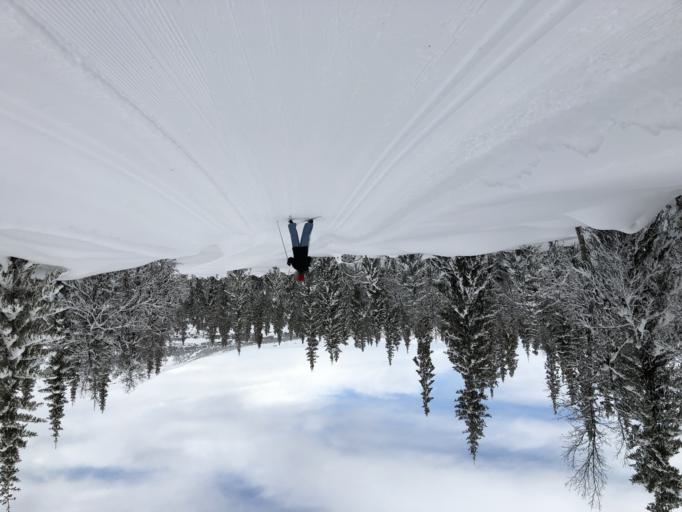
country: NO
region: Oppland
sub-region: Gausdal
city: Segalstad bru
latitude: 61.3249
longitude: 10.0779
